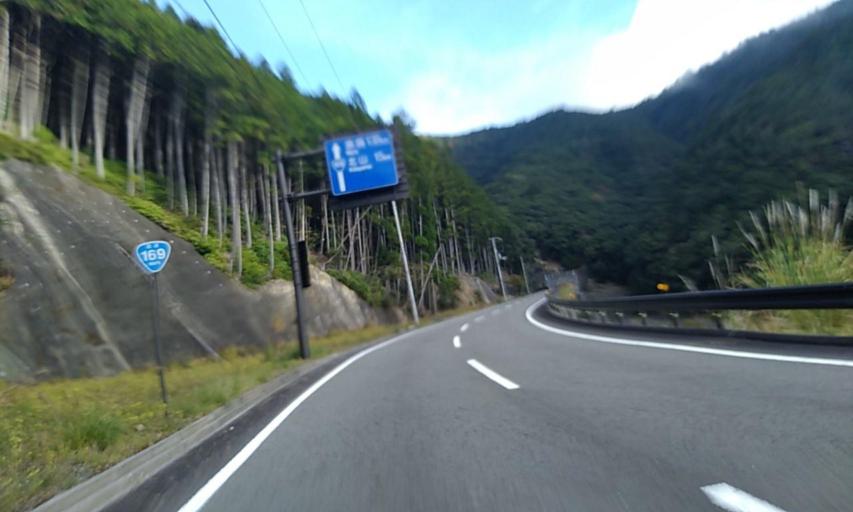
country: JP
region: Wakayama
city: Shingu
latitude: 33.8782
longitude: 135.8762
